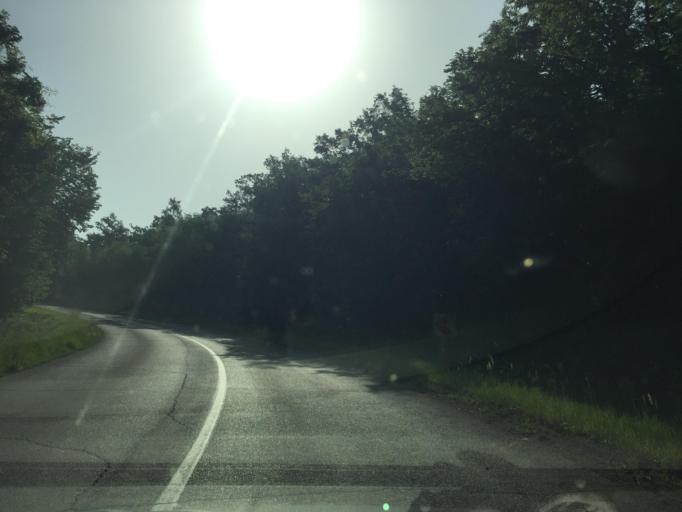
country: HR
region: Primorsko-Goranska
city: Klana
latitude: 45.4281
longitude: 14.3617
